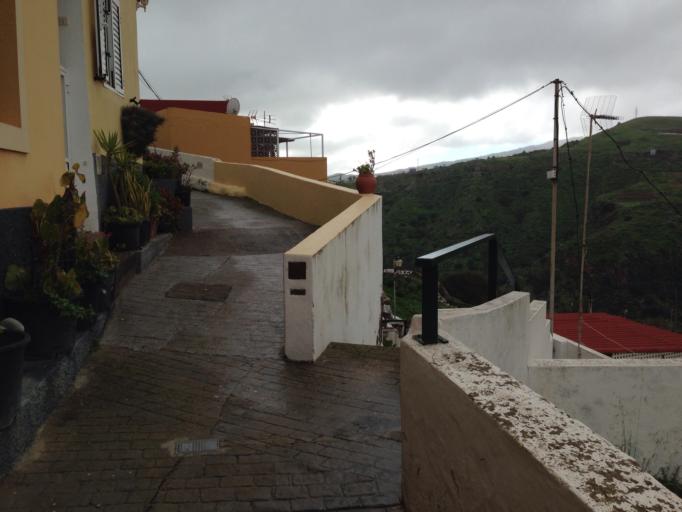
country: ES
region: Canary Islands
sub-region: Provincia de Las Palmas
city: Santa Brigida
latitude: 28.0269
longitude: -15.4785
